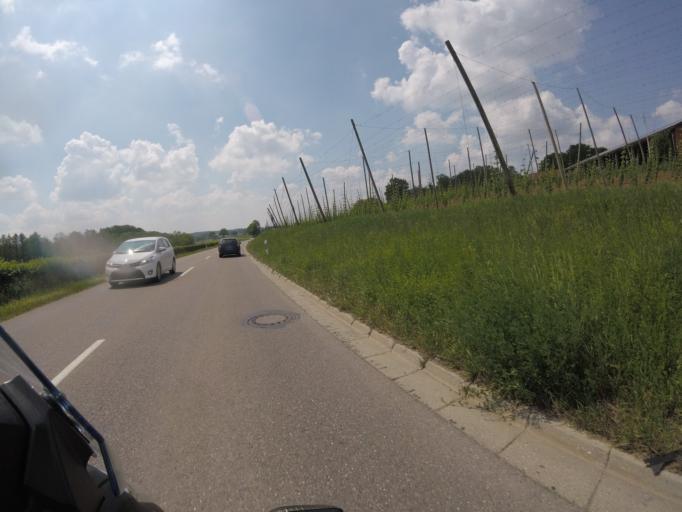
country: DE
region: Bavaria
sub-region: Upper Bavaria
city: Scheyern
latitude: 48.5114
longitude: 11.4596
